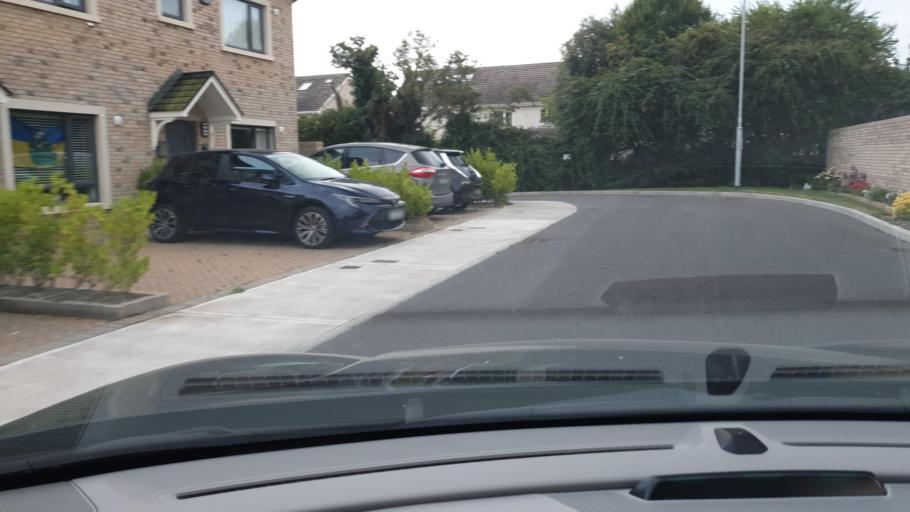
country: IE
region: Leinster
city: Donabate
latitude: 53.4951
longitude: -6.1426
